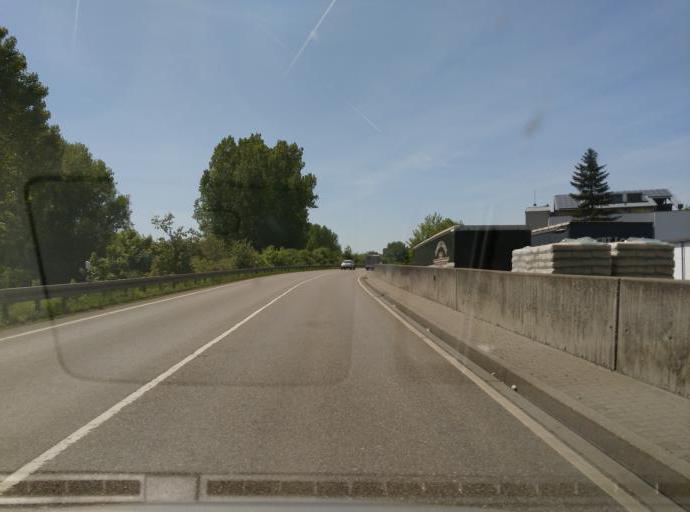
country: DE
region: Baden-Wuerttemberg
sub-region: Regierungsbezirk Stuttgart
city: Neckartailfingen
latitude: 48.6078
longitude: 9.2625
